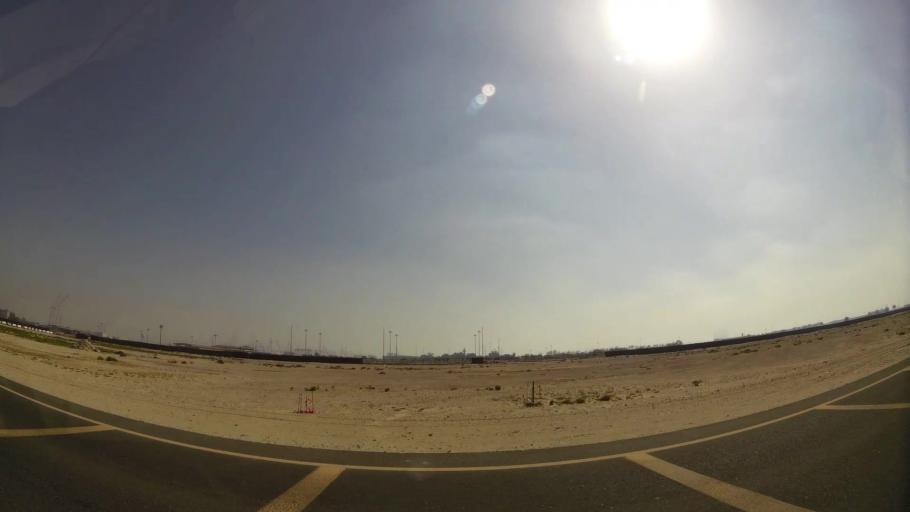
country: AE
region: Dubai
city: Dubai
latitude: 24.9600
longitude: 55.0446
